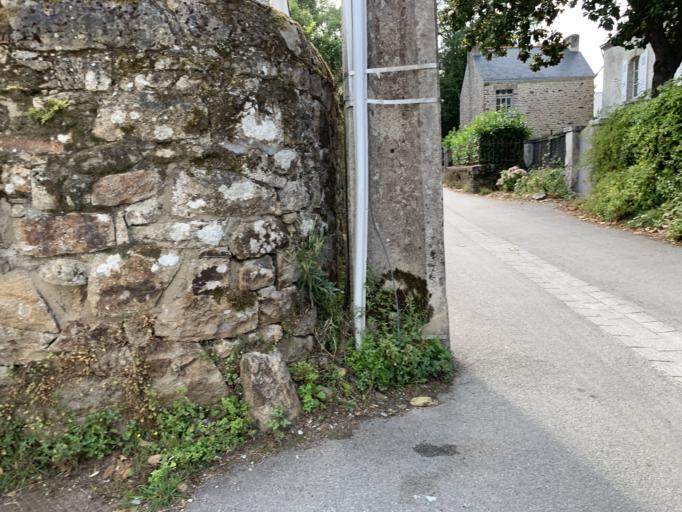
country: FR
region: Brittany
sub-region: Departement du Morbihan
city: Arradon
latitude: 47.5956
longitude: -2.8479
